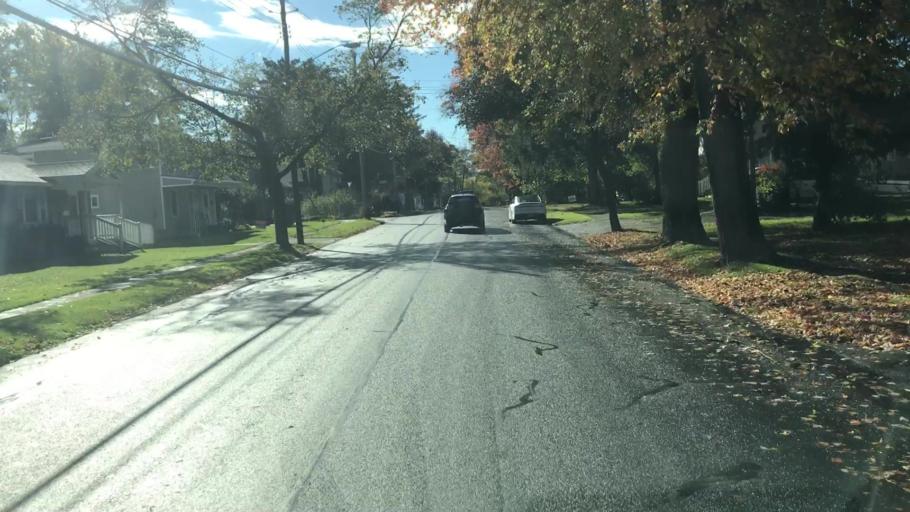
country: US
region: New York
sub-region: Cayuga County
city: Auburn
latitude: 42.9241
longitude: -76.5541
